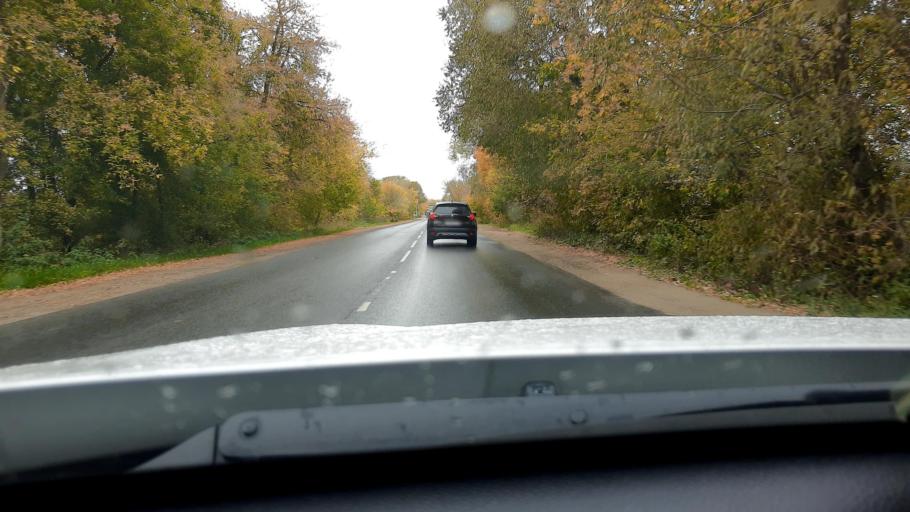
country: RU
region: Moskovskaya
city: Domodedovo
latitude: 55.4324
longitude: 37.7270
